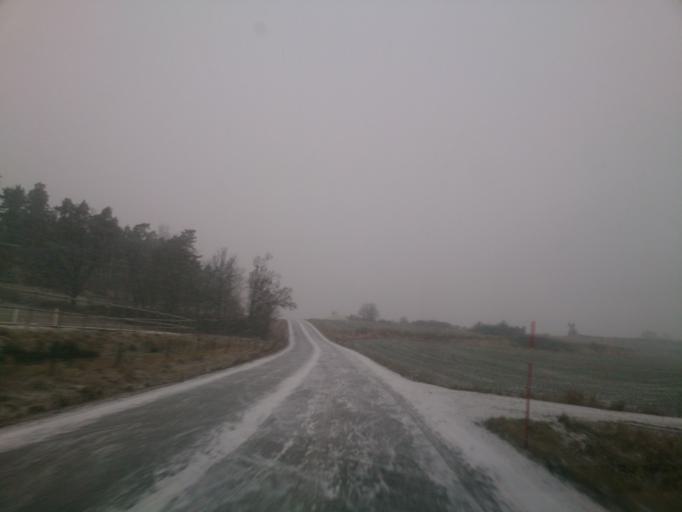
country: SE
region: OEstergoetland
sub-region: Soderkopings Kommun
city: Soederkoeping
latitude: 58.4868
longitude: 16.2972
